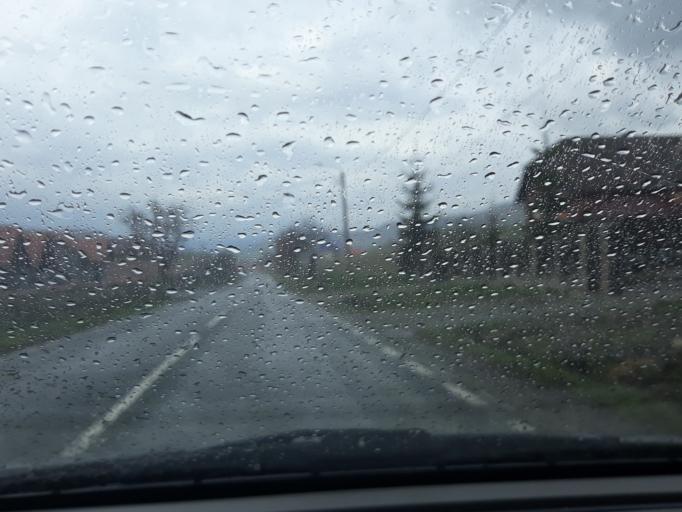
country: RO
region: Harghita
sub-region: Comuna Corund
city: Corund
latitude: 46.4822
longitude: 25.1718
